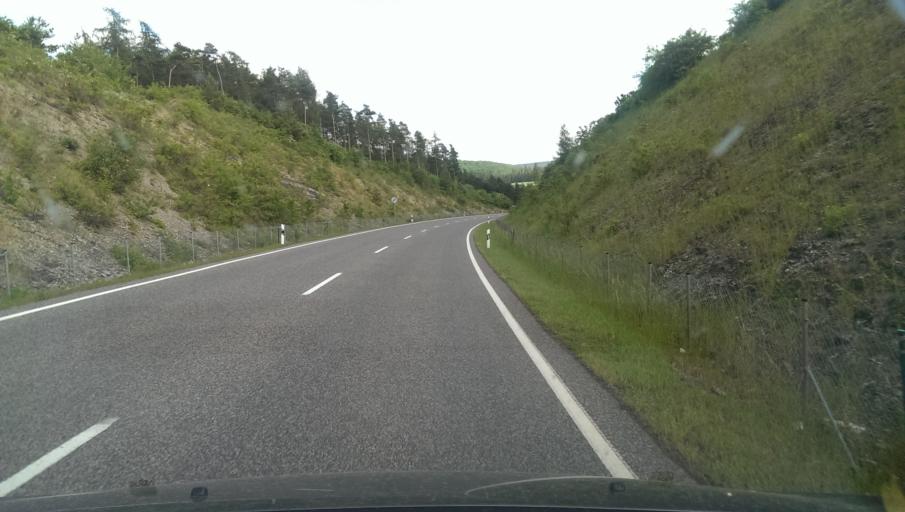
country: DE
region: Thuringia
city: Geschwenda
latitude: 50.7393
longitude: 10.8317
